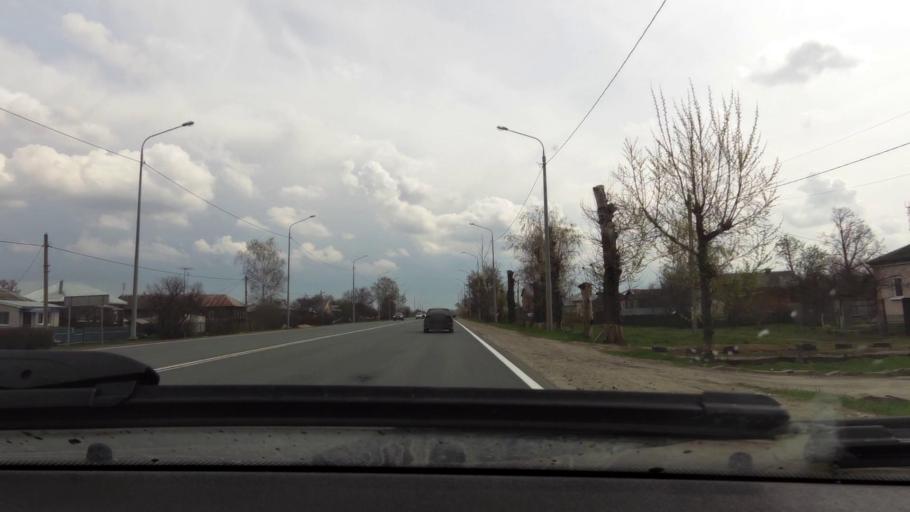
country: RU
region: Rjazan
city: Bagramovo
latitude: 54.7504
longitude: 39.4249
